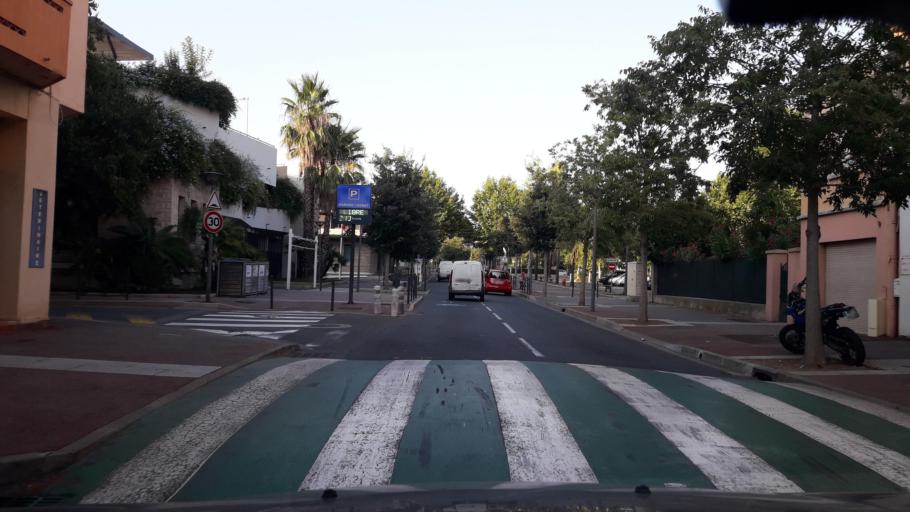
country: FR
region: Provence-Alpes-Cote d'Azur
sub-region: Departement du Var
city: Saint-Raphael
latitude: 43.4271
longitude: 6.7704
